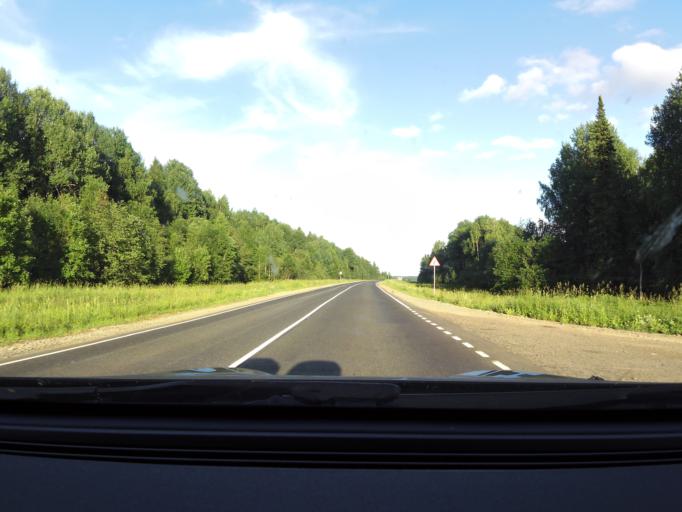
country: RU
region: Kirov
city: Kostino
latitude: 58.8149
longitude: 53.5860
